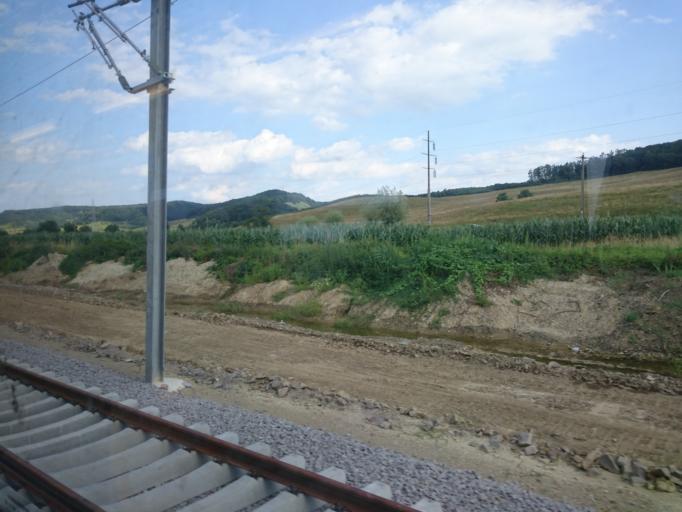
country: RO
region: Sibiu
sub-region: Comuna Alma
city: Alma
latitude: 46.2027
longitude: 24.4927
